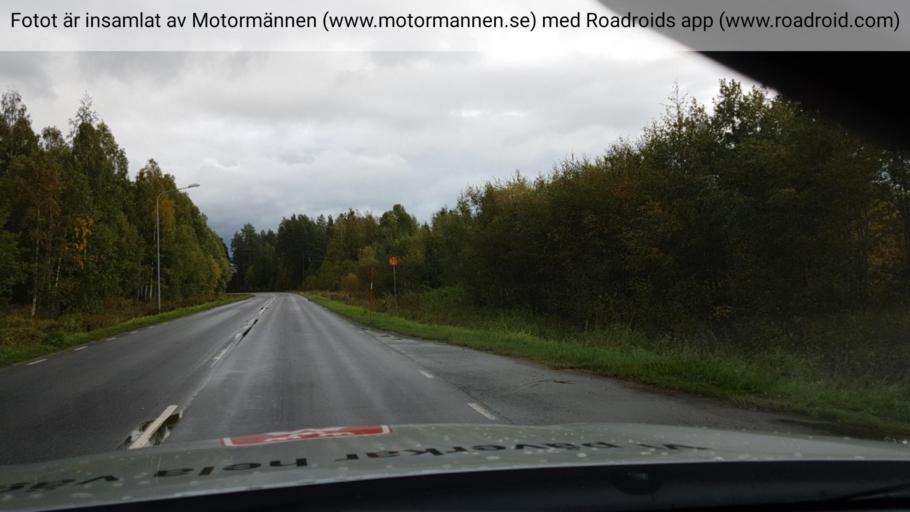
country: SE
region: Norrbotten
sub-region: Bodens Kommun
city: Boden
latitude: 65.8146
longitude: 21.6222
